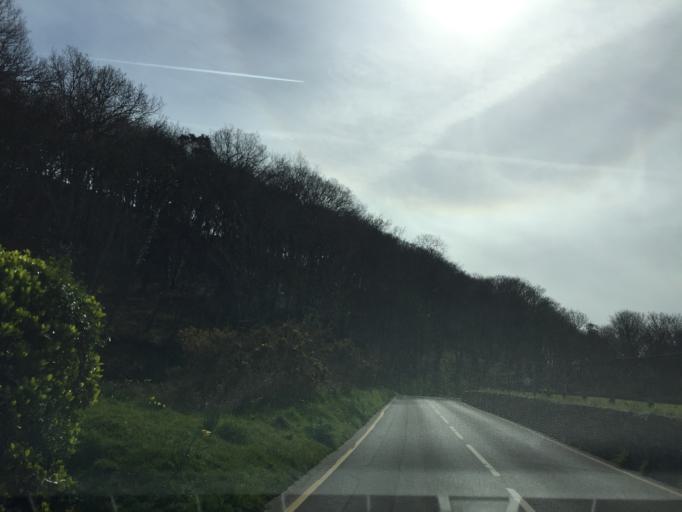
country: JE
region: St Helier
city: Saint Helier
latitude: 49.2452
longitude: -2.2018
